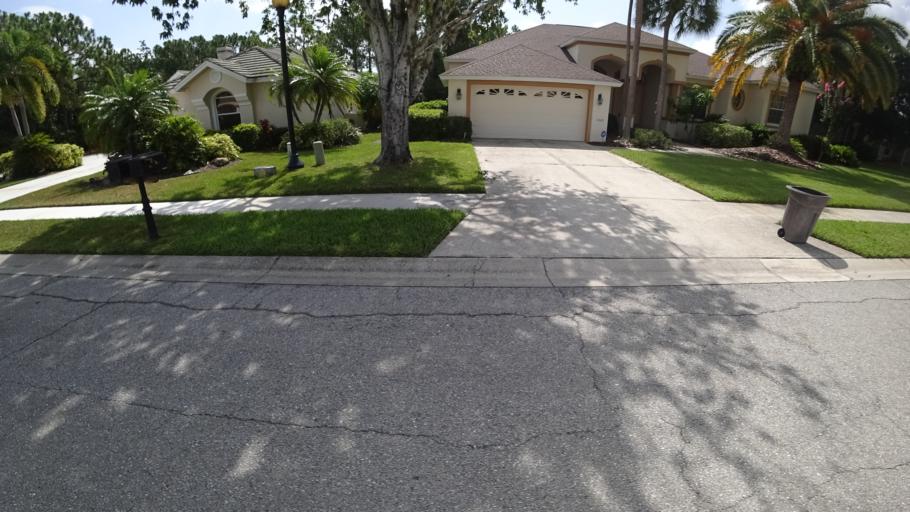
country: US
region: Florida
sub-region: Sarasota County
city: The Meadows
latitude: 27.4111
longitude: -82.4432
